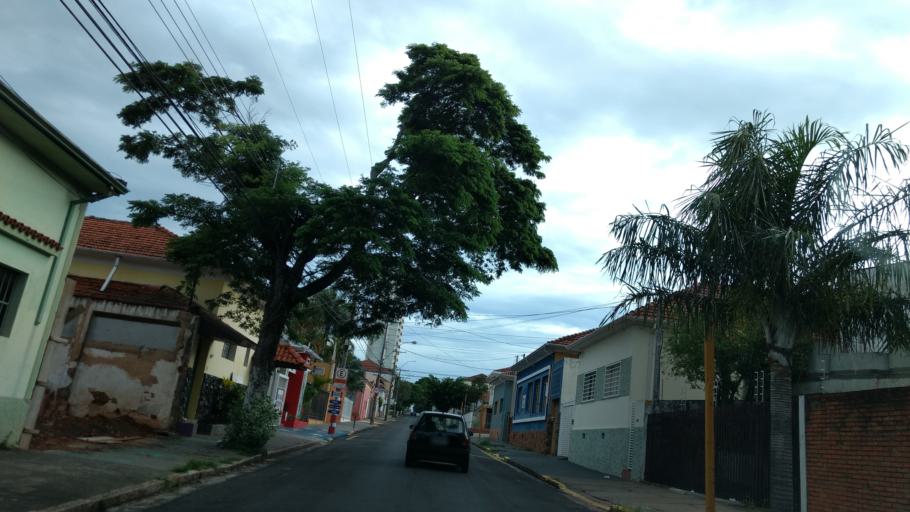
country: BR
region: Sao Paulo
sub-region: Botucatu
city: Botucatu
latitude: -22.8894
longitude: -48.4428
